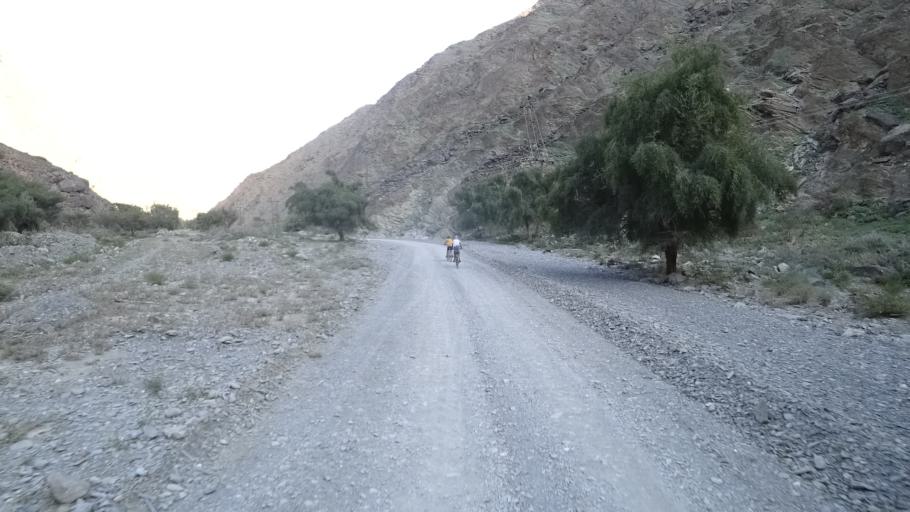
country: OM
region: Al Batinah
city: Bayt al `Awabi
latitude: 23.2539
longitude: 57.3974
